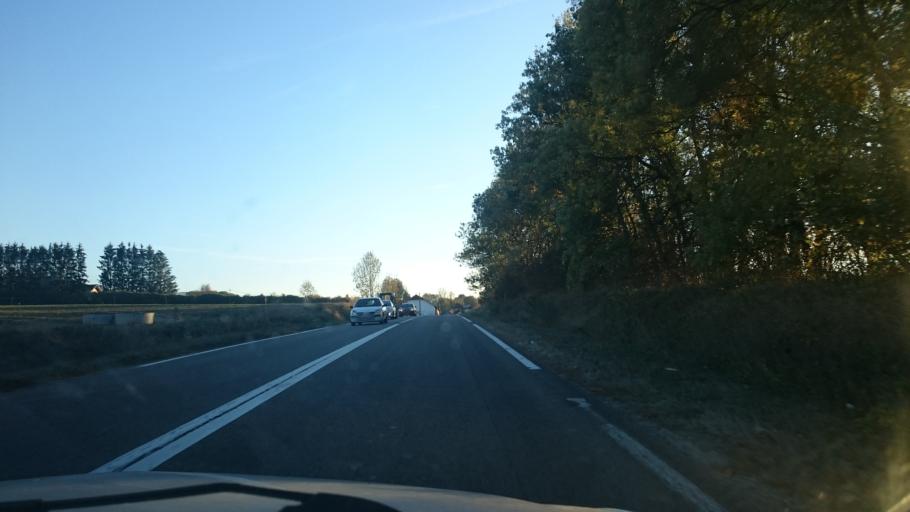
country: FR
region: Franche-Comte
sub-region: Departement du Doubs
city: Quingey
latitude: 47.0561
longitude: 5.8808
